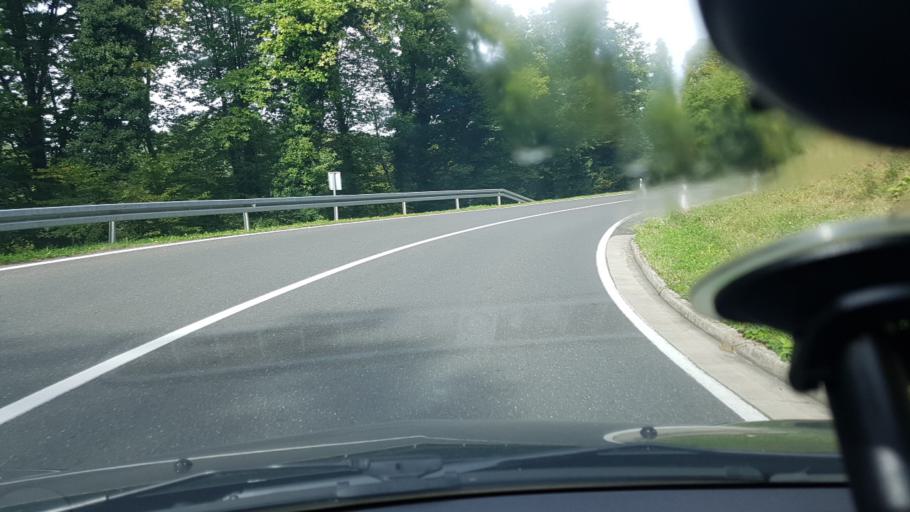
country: HR
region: Varazdinska
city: Ljubescica
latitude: 46.1279
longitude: 16.3566
